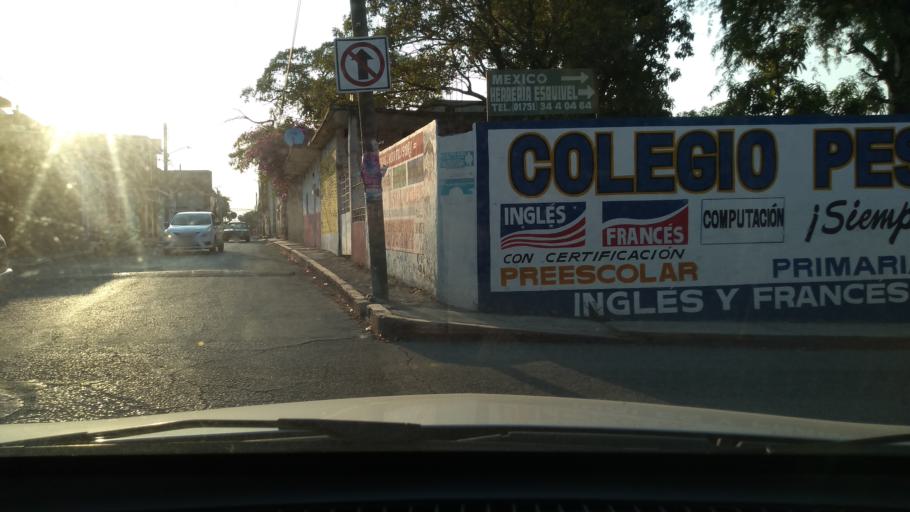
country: MX
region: Morelos
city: Puente de Ixtla
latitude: 18.6227
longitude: -99.3209
